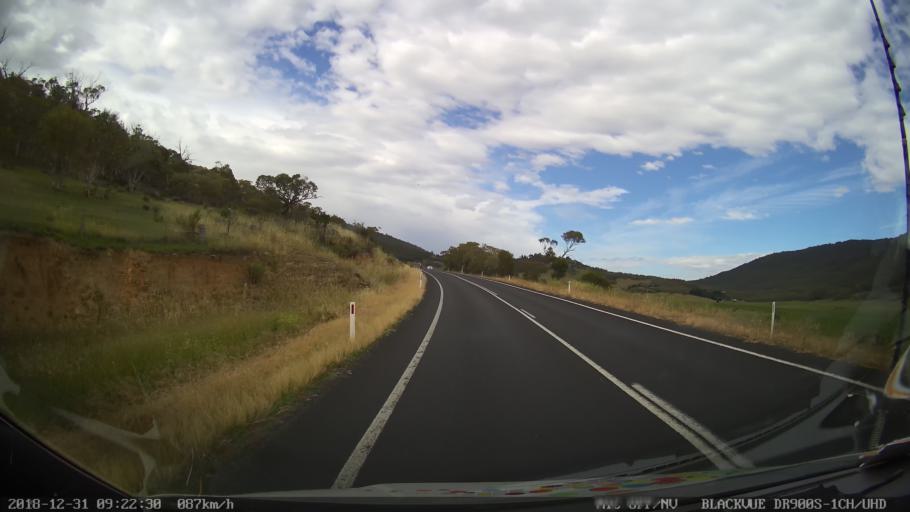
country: AU
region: New South Wales
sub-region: Snowy River
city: Jindabyne
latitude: -36.4344
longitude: 148.5461
